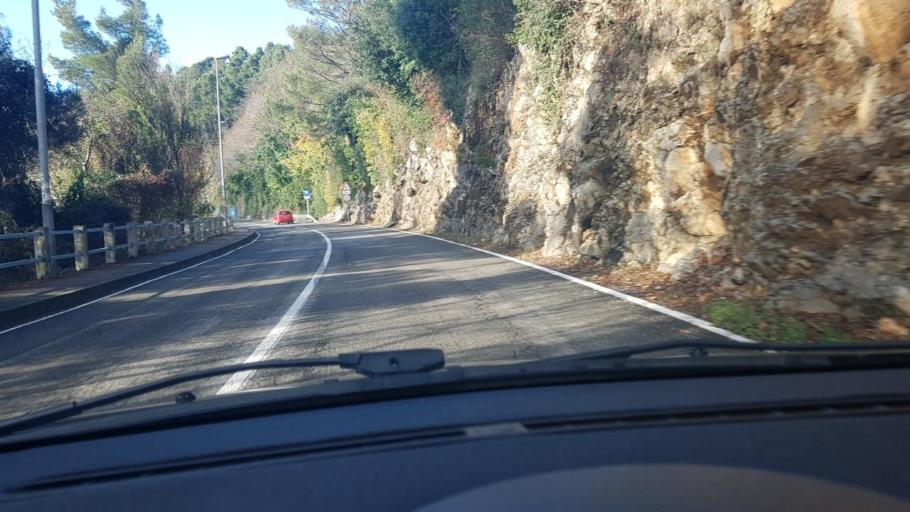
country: HR
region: Primorsko-Goranska
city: Matulji
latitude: 45.3565
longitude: 14.3299
